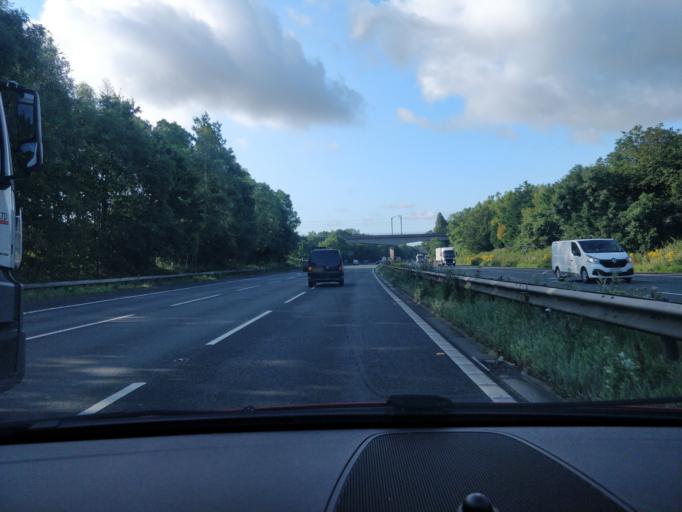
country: GB
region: England
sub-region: Knowsley
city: Prescot
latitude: 53.4196
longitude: -2.8138
